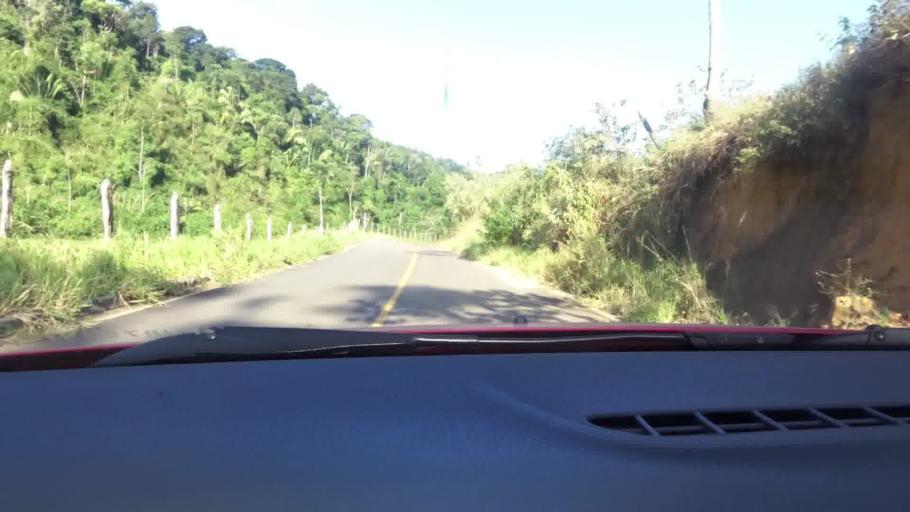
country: BR
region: Espirito Santo
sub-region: Guarapari
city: Guarapari
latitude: -20.5641
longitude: -40.5495
